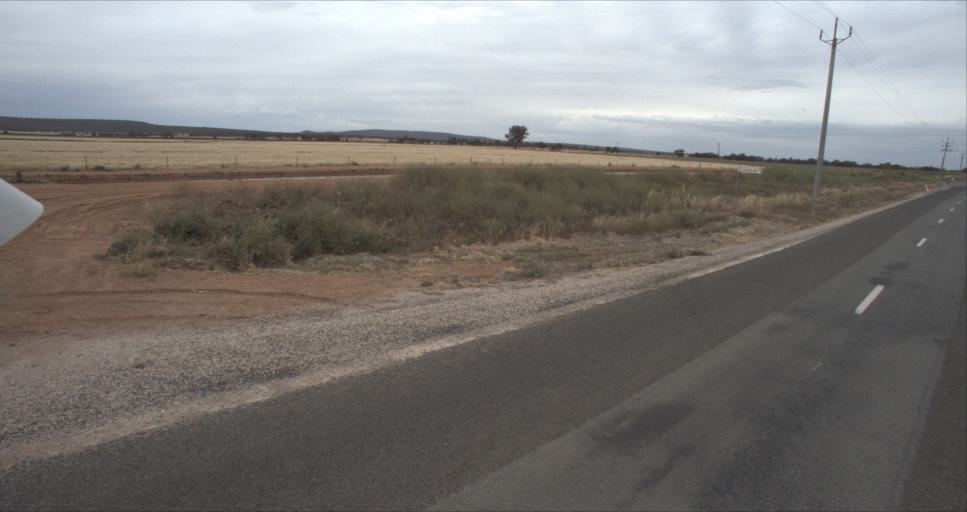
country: AU
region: New South Wales
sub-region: Leeton
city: Leeton
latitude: -34.4773
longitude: 146.3975
